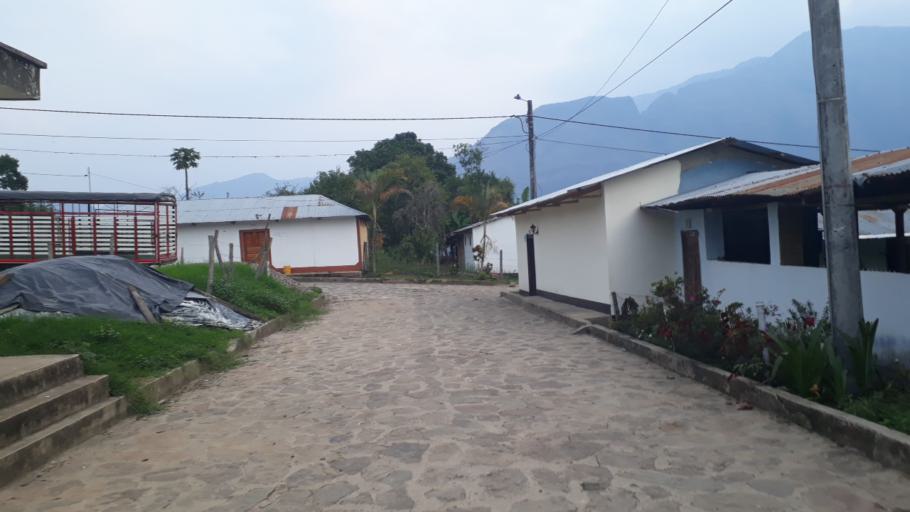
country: CO
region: Casanare
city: Nunchia
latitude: 5.6242
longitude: -72.4246
